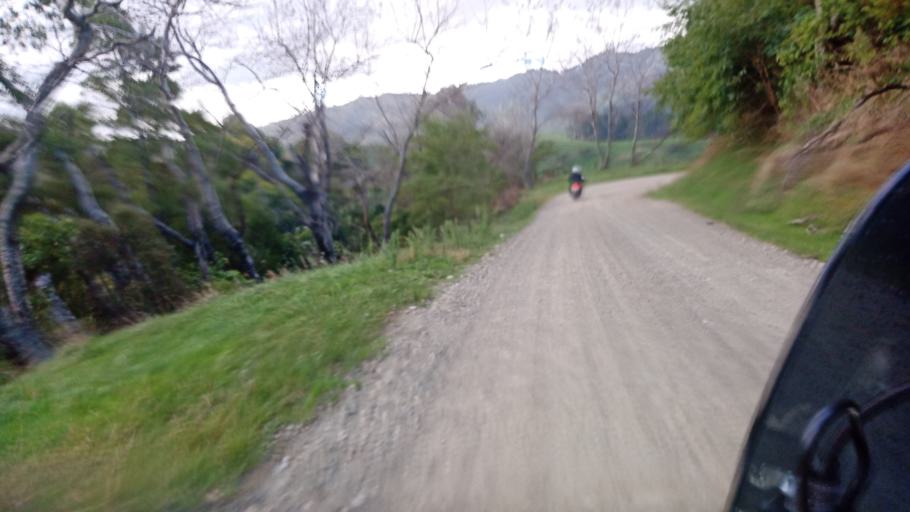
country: NZ
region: Gisborne
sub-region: Gisborne District
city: Gisborne
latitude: -38.4633
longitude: 177.6300
